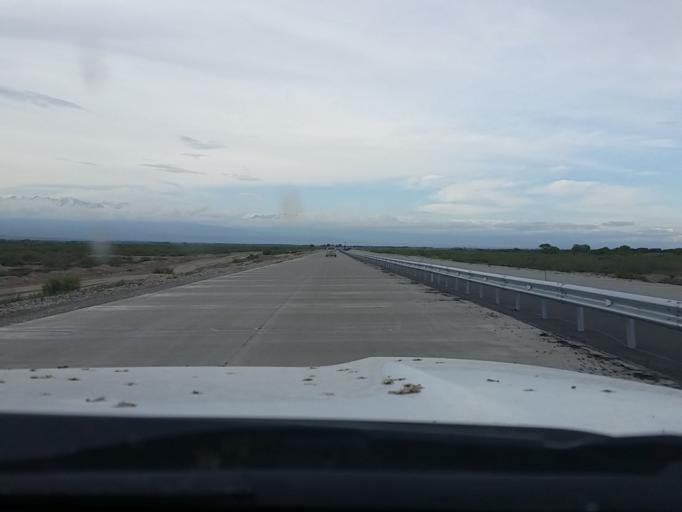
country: KZ
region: Almaty Oblysy
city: Zharkent
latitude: 44.0858
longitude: 80.0497
